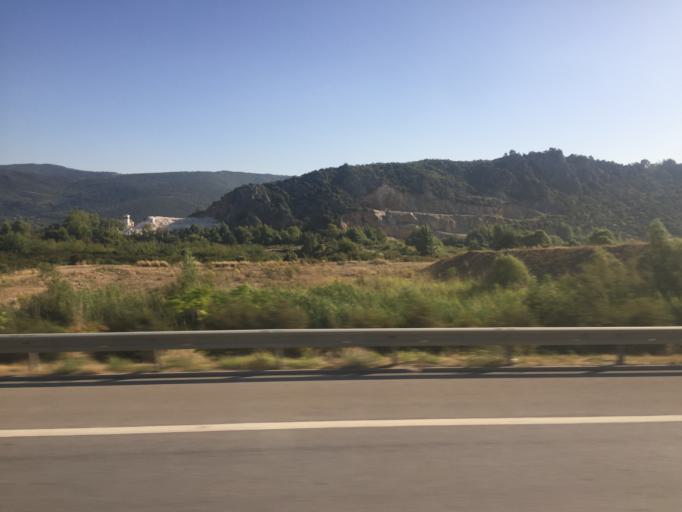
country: TR
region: Bursa
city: Kestel
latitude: 40.2031
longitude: 29.3098
